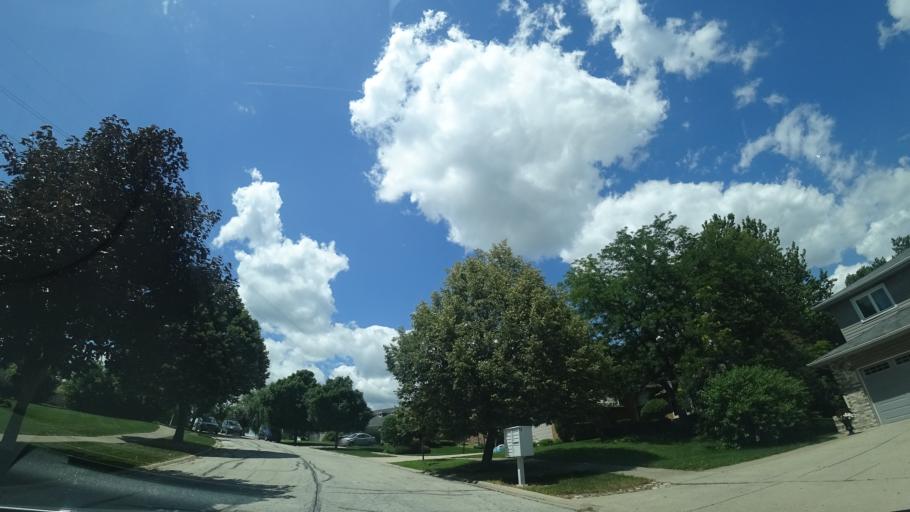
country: US
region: Illinois
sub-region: Will County
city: Homer Glen
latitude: 41.5781
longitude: -87.8994
